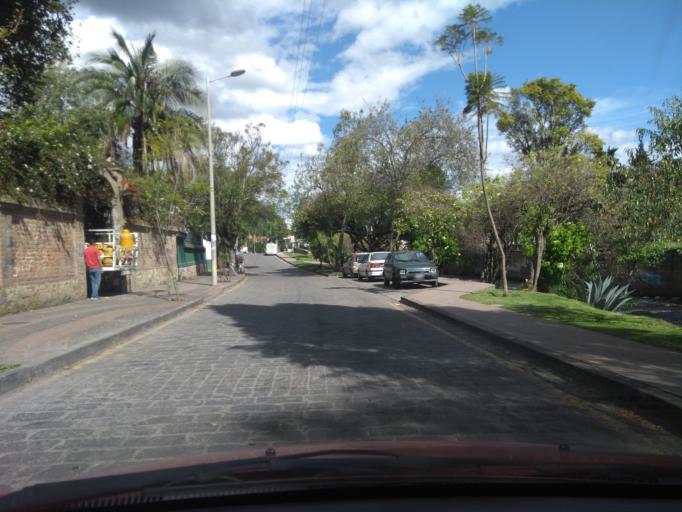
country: EC
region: Azuay
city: Cuenca
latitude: -2.9025
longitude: -79.0040
